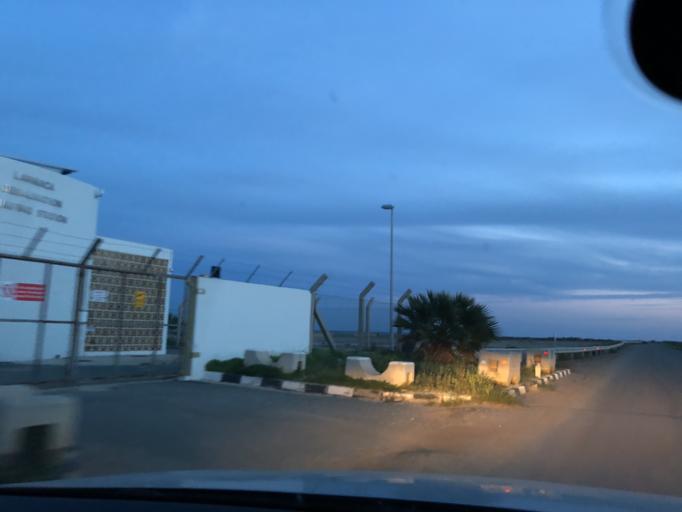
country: CY
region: Larnaka
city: Meneou
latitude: 34.8687
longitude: 33.6378
